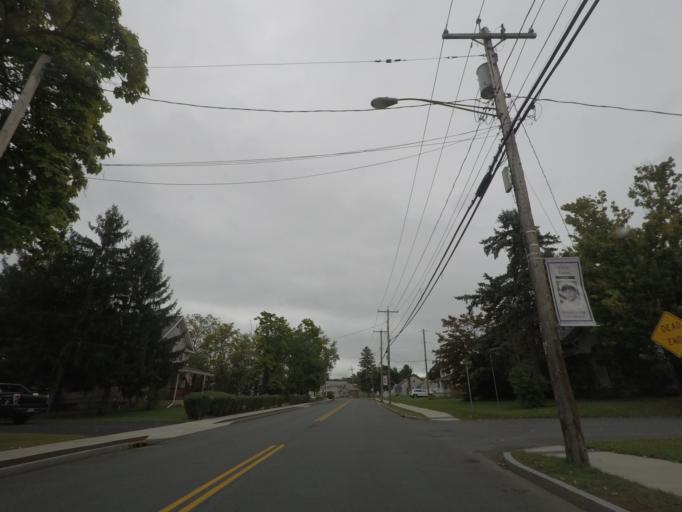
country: US
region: New York
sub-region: Rensselaer County
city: Rensselaer
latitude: 42.6559
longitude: -73.7101
